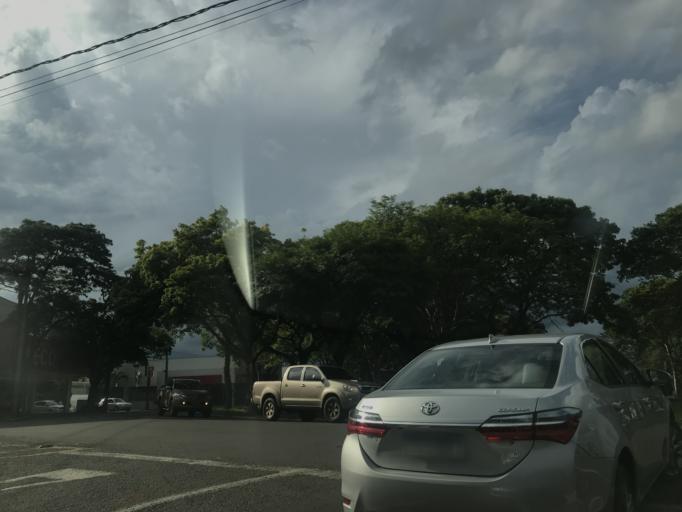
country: BR
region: Parana
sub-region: Maringa
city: Maringa
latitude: -23.4270
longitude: -51.9643
